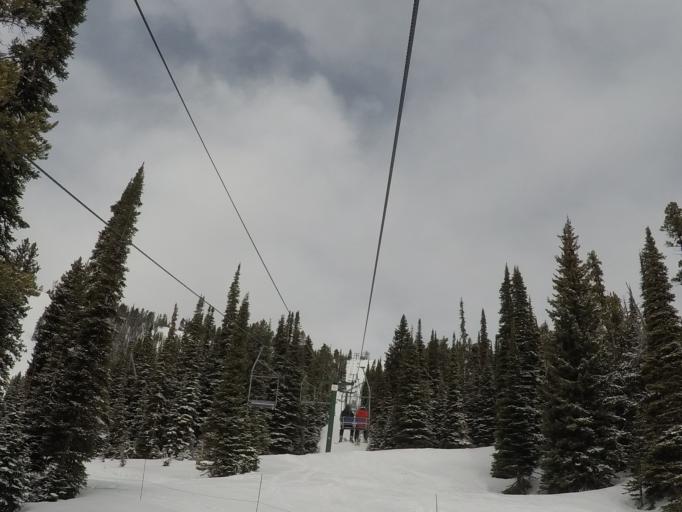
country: US
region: Montana
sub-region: Meagher County
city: White Sulphur Springs
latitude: 46.8340
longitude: -110.7103
